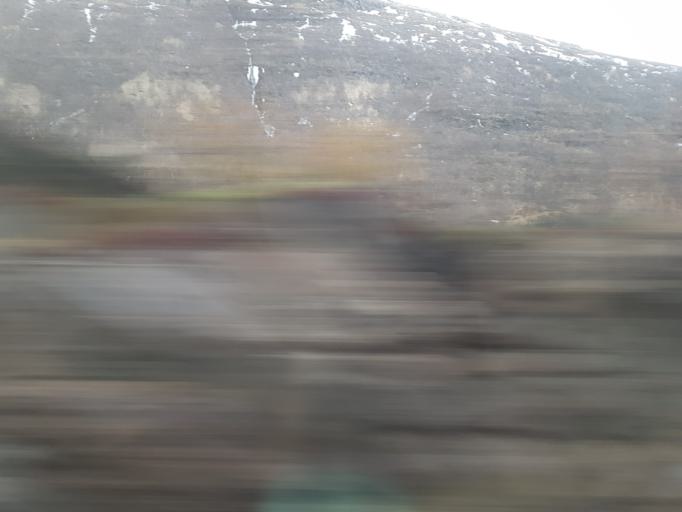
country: NO
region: Sor-Trondelag
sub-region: Oppdal
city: Oppdal
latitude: 62.3234
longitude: 9.6191
